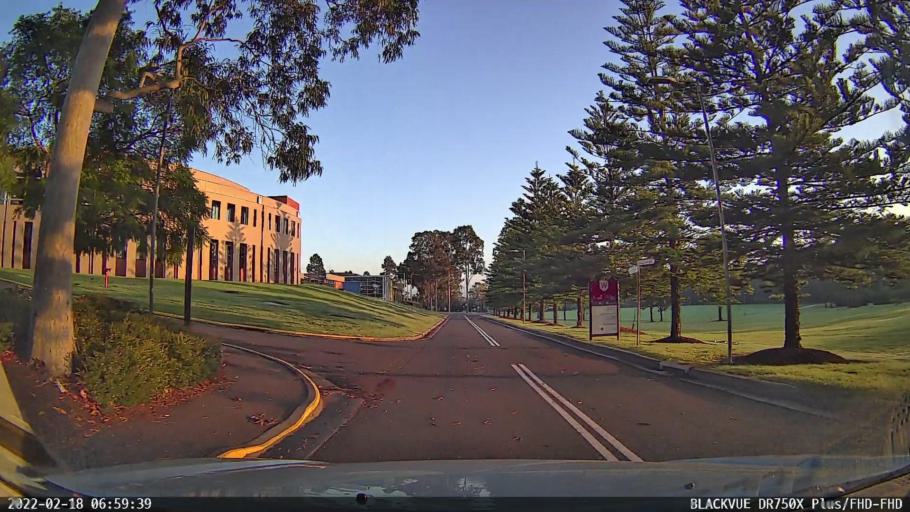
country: AU
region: New South Wales
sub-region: Penrith Municipality
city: Kingswood Park
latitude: -33.7675
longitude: 150.7303
